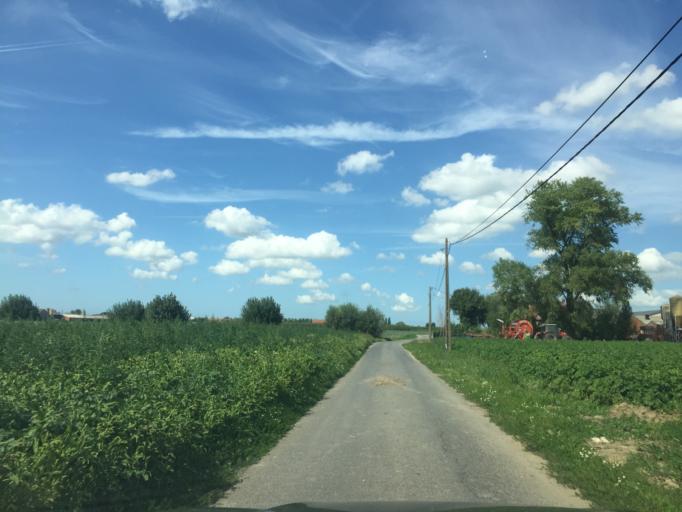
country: BE
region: Flanders
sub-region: Provincie West-Vlaanderen
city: Hooglede
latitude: 50.9947
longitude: 3.0556
